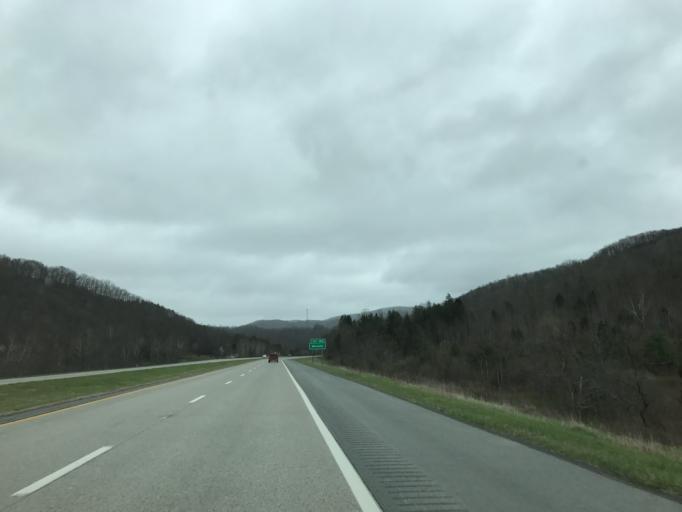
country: US
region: West Virginia
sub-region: Summers County
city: Hinton
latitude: 37.7985
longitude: -80.8428
